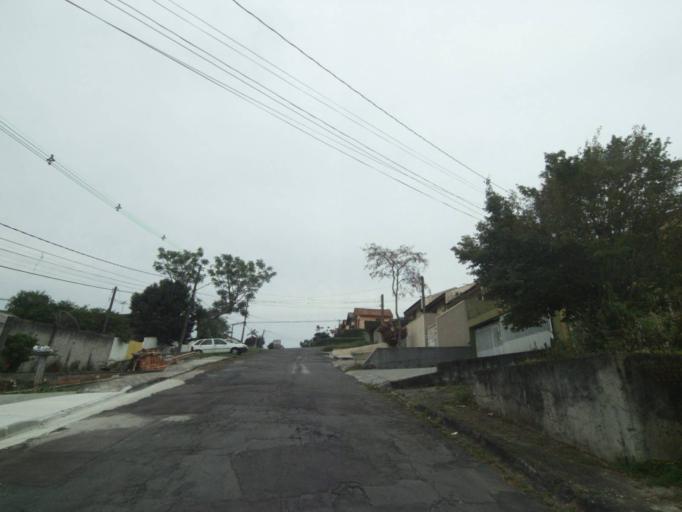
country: BR
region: Parana
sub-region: Pinhais
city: Pinhais
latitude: -25.4088
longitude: -49.1990
